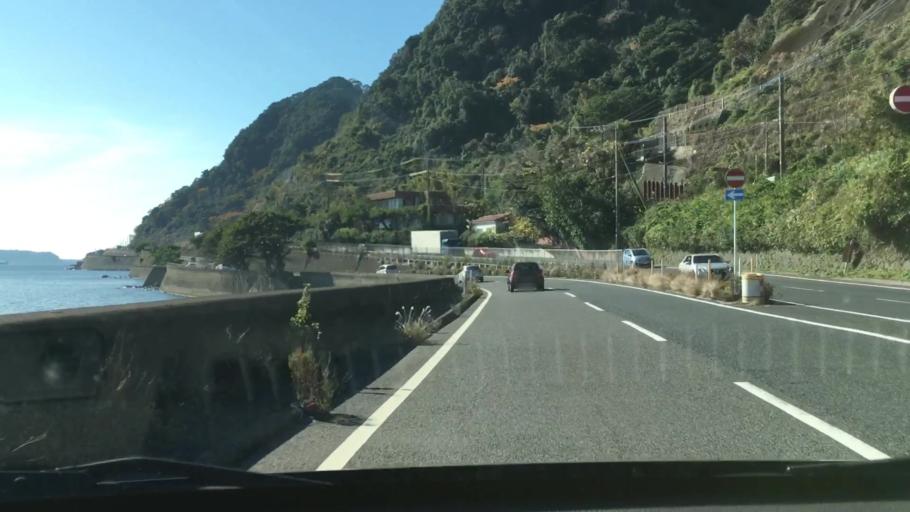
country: JP
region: Kagoshima
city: Kagoshima-shi
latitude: 31.6456
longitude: 130.6035
